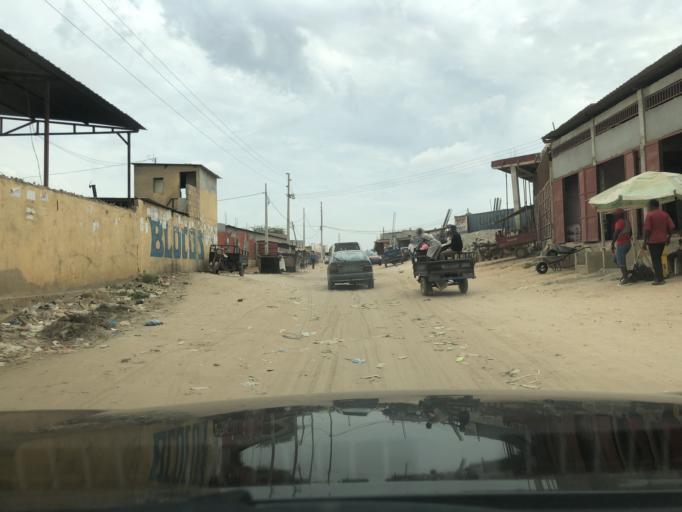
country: AO
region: Luanda
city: Luanda
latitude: -8.9260
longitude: 13.2291
